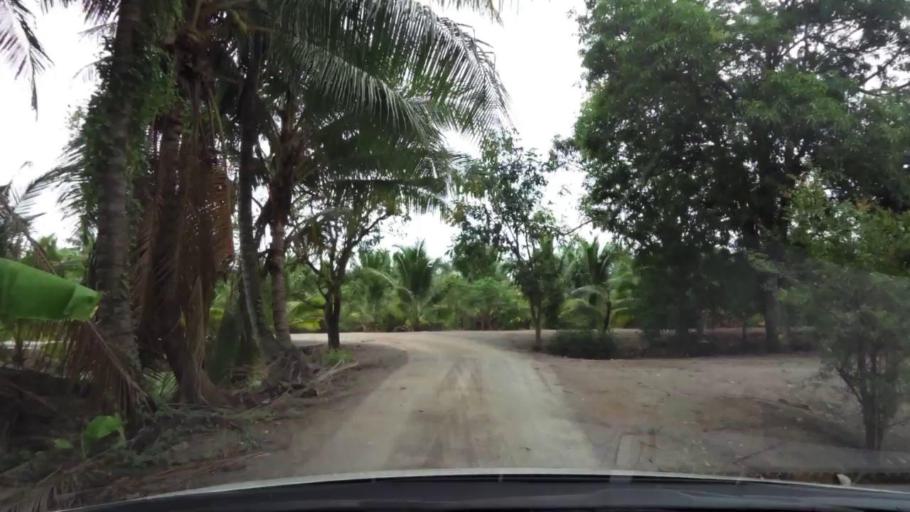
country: TH
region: Ratchaburi
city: Damnoen Saduak
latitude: 13.5545
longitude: 99.9875
